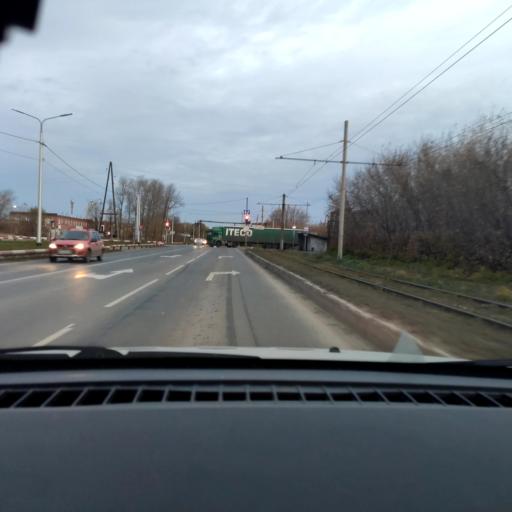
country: RU
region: Perm
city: Kondratovo
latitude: 57.9252
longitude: 56.1373
